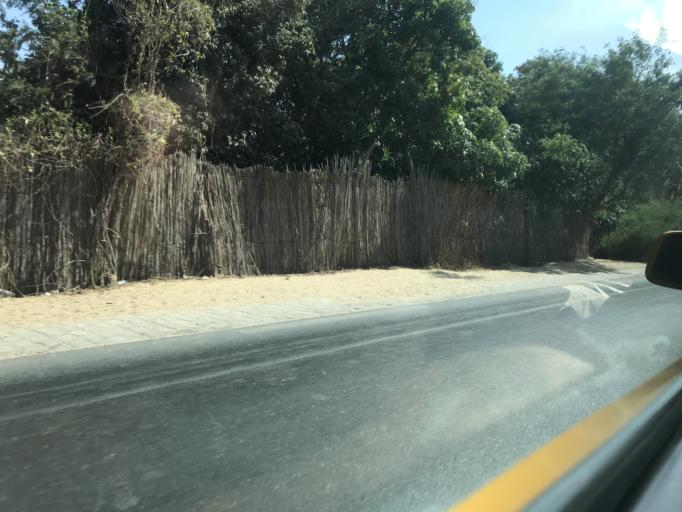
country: SN
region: Saint-Louis
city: Saint-Louis
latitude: 16.0382
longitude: -16.4594
